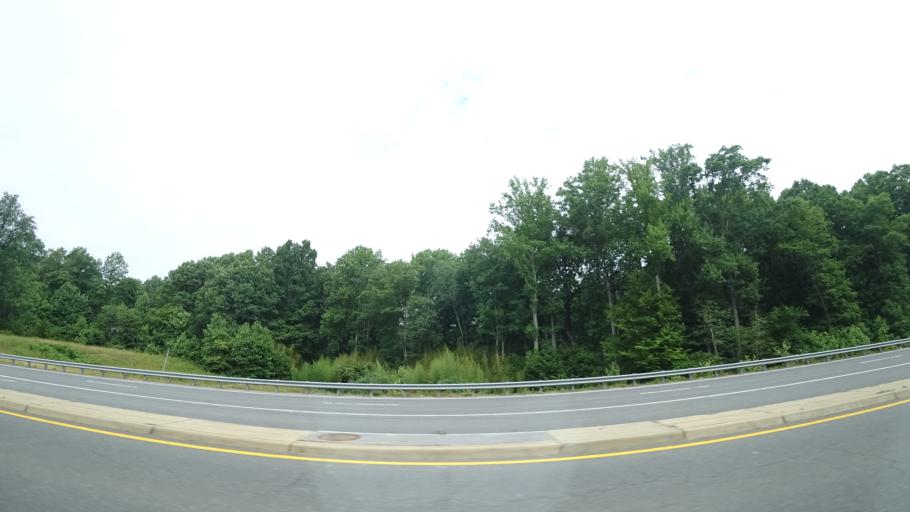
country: US
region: Virginia
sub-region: Spotsylvania County
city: Spotsylvania
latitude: 38.2027
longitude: -77.6047
